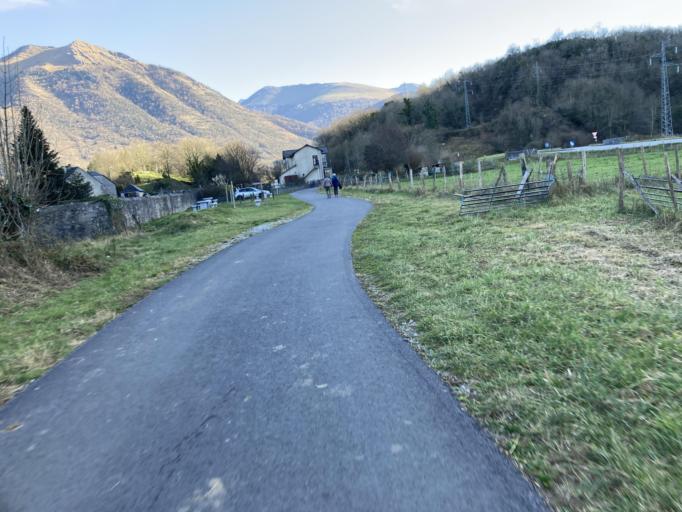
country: FR
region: Aquitaine
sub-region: Departement des Pyrenees-Atlantiques
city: Louvie-Juzon
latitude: 43.0915
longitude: -0.4301
